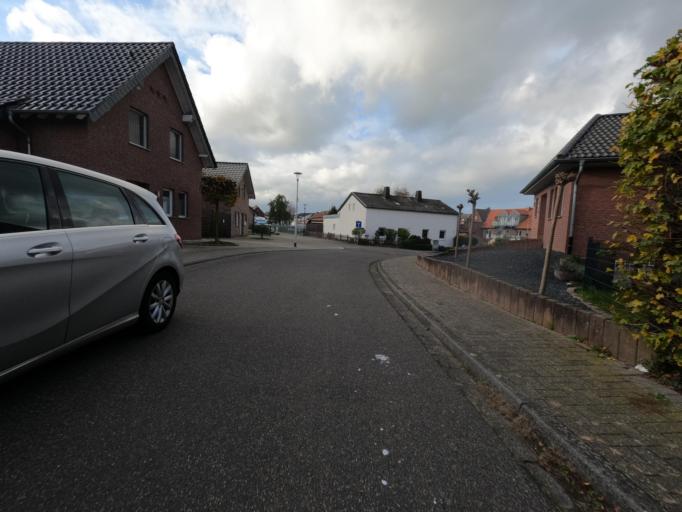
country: DE
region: North Rhine-Westphalia
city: Geilenkirchen
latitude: 50.9675
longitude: 6.1080
